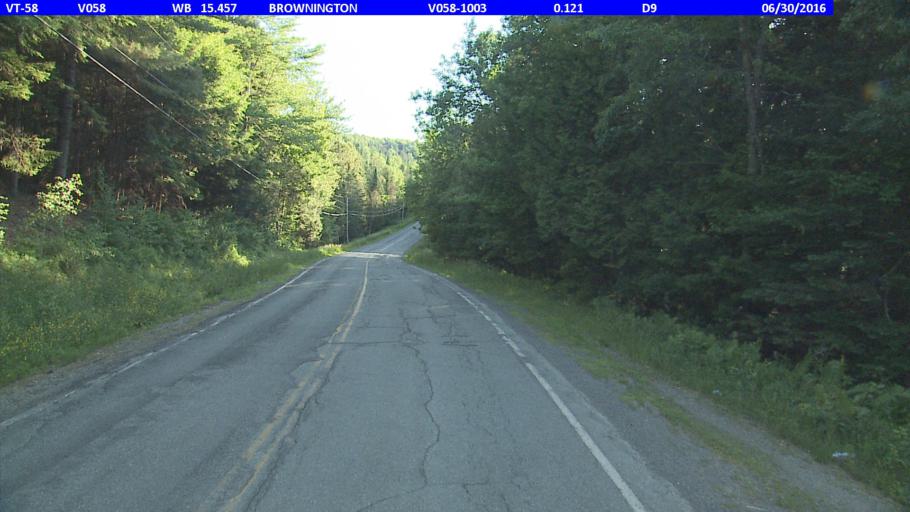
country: US
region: Vermont
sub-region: Orleans County
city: Newport
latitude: 44.8056
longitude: -72.1422
